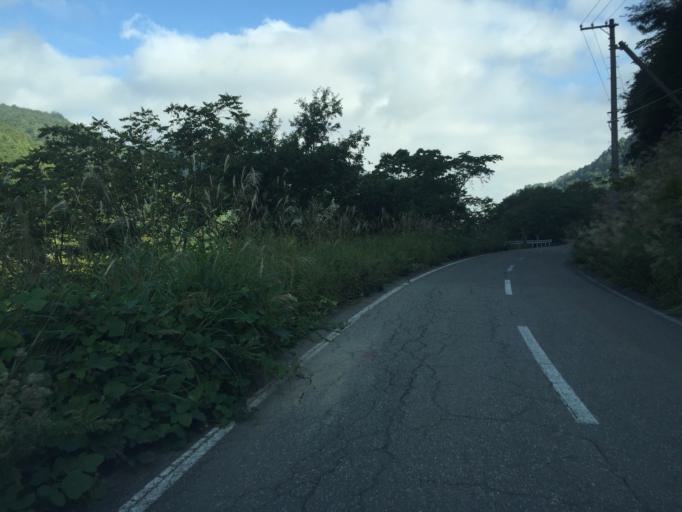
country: JP
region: Fukushima
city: Inawashiro
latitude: 37.4437
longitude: 139.9675
